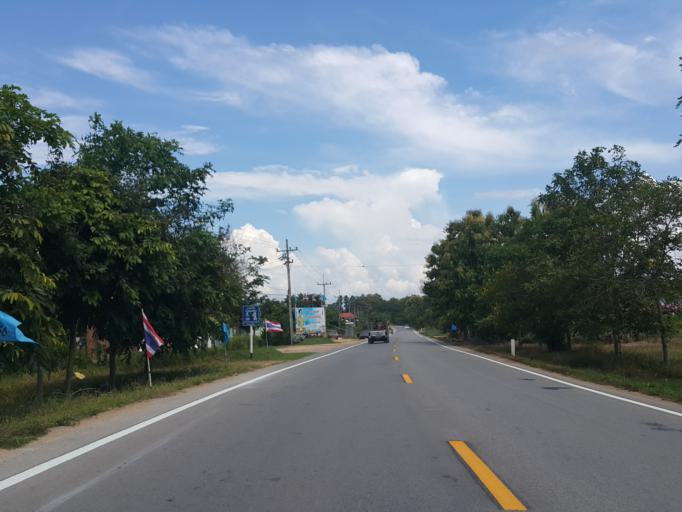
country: TH
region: Chiang Mai
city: Phrao
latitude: 19.2496
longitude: 99.1842
